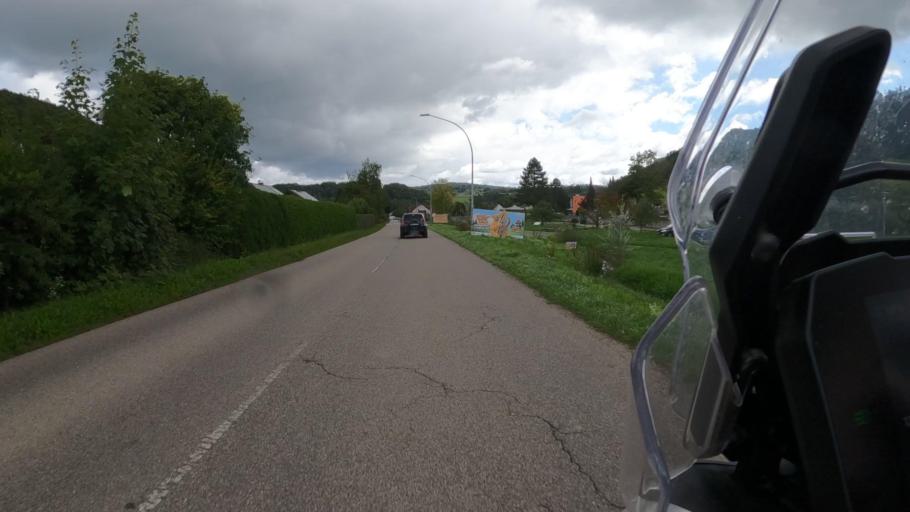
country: DE
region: Baden-Wuerttemberg
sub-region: Freiburg Region
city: Eggingen
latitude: 47.6998
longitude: 8.3884
